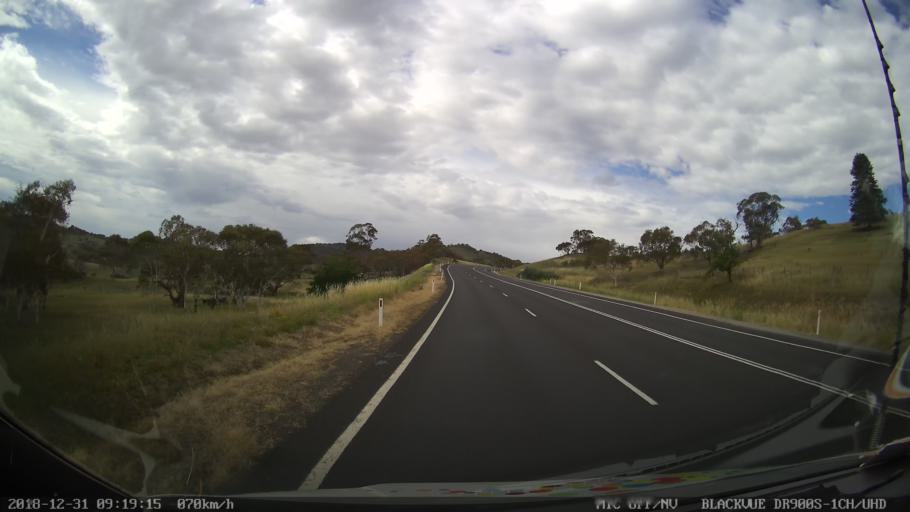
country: AU
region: New South Wales
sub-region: Snowy River
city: Jindabyne
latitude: -36.4139
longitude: 148.5870
